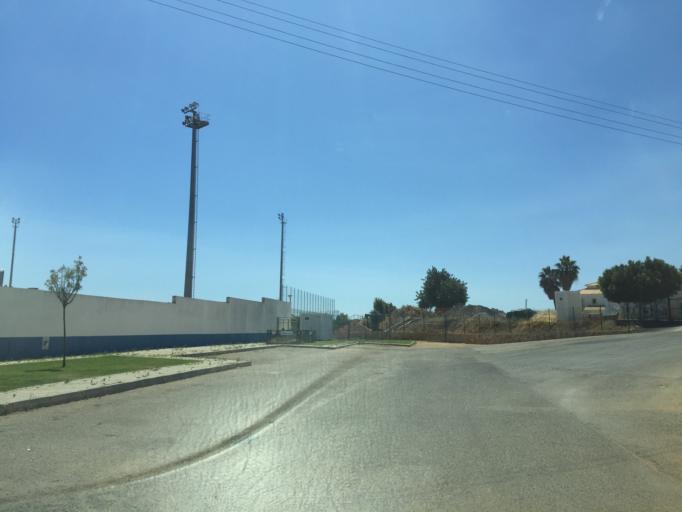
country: PT
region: Faro
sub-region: Albufeira
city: Ferreiras
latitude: 37.1245
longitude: -8.2435
